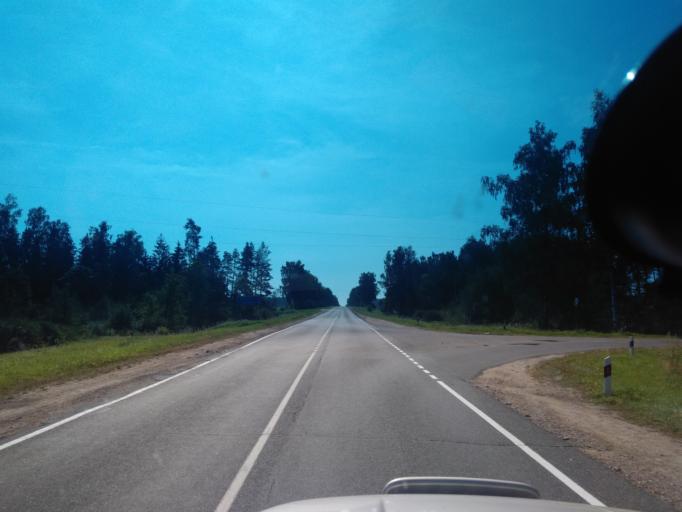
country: BY
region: Minsk
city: Uzda
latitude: 53.3532
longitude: 27.2257
